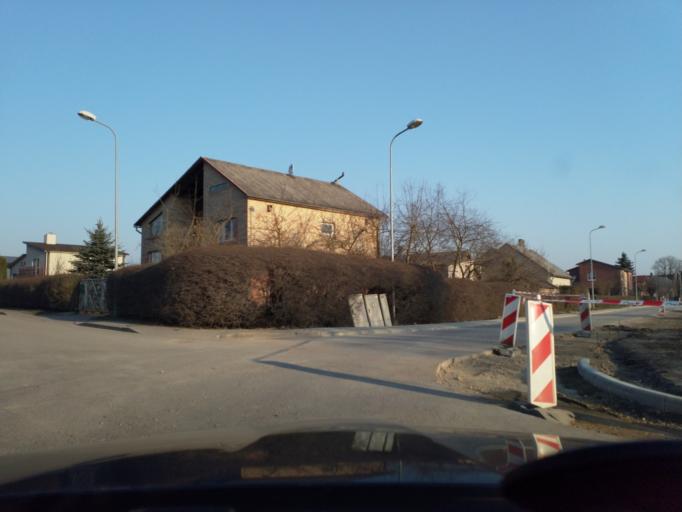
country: LV
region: Grobina
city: Grobina
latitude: 56.5309
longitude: 21.1826
